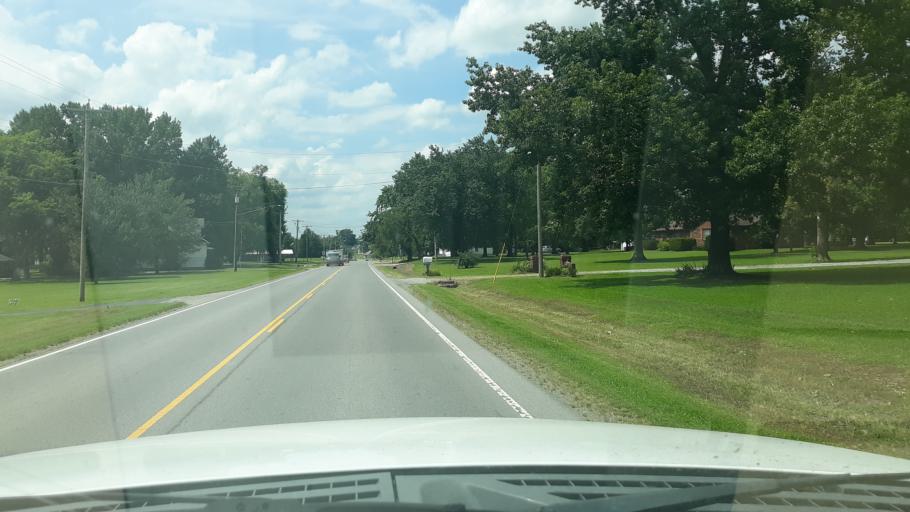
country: US
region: Illinois
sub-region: Saline County
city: Eldorado
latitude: 37.8260
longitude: -88.5242
